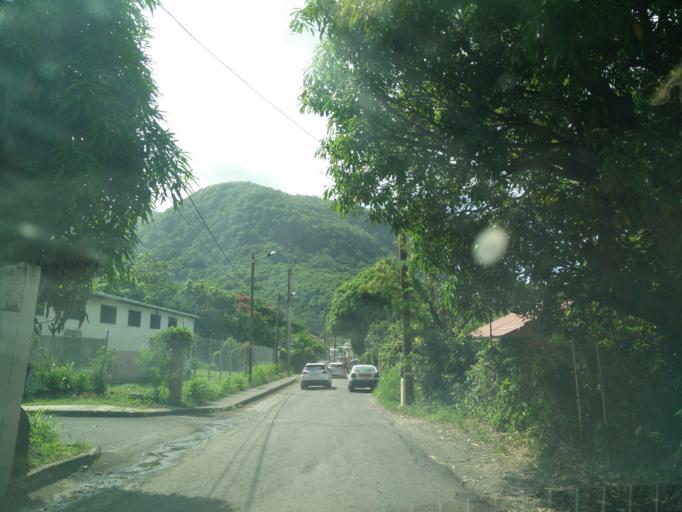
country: GP
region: Guadeloupe
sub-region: Guadeloupe
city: Basse-Terre
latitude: 15.9883
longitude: -61.7102
